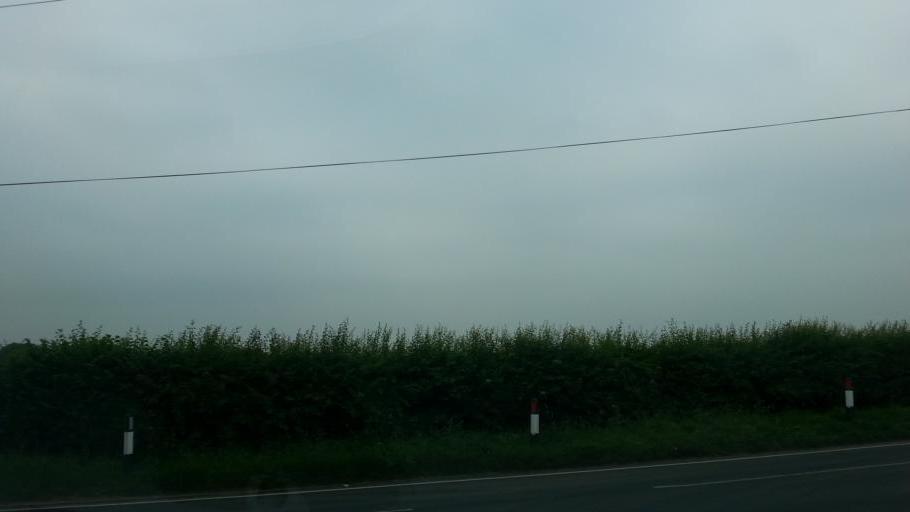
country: GB
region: England
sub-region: Staffordshire
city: Uttoxeter
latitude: 52.8292
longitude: -1.8998
